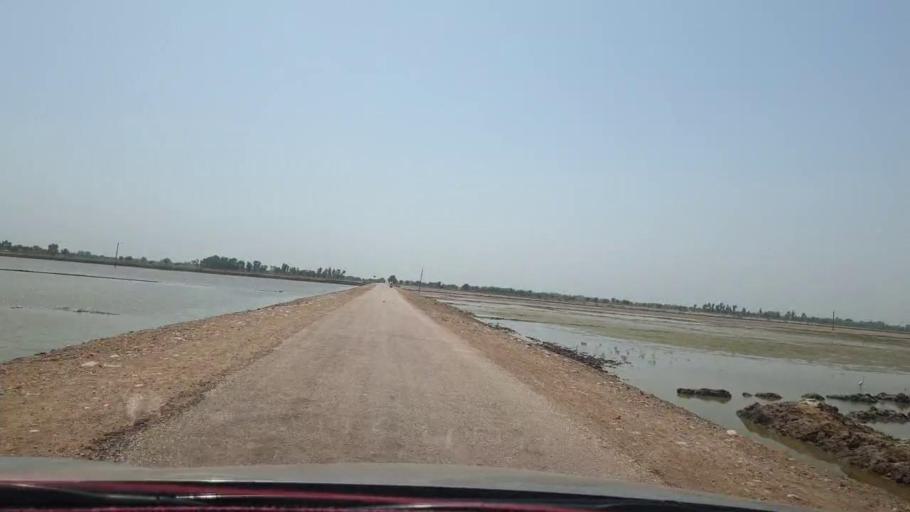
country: PK
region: Sindh
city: Warah
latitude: 27.5479
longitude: 67.7945
